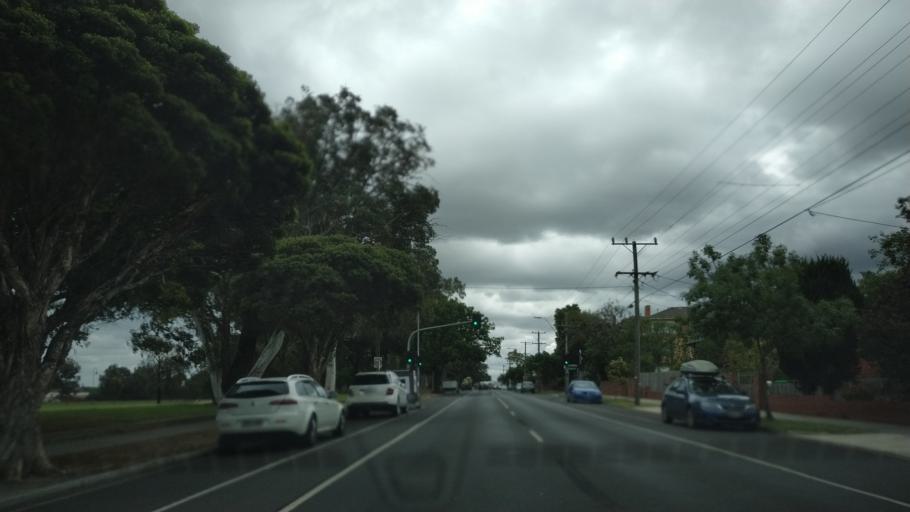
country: AU
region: Victoria
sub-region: Glen Eira
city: Caulfield South
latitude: -37.8954
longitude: 145.0273
